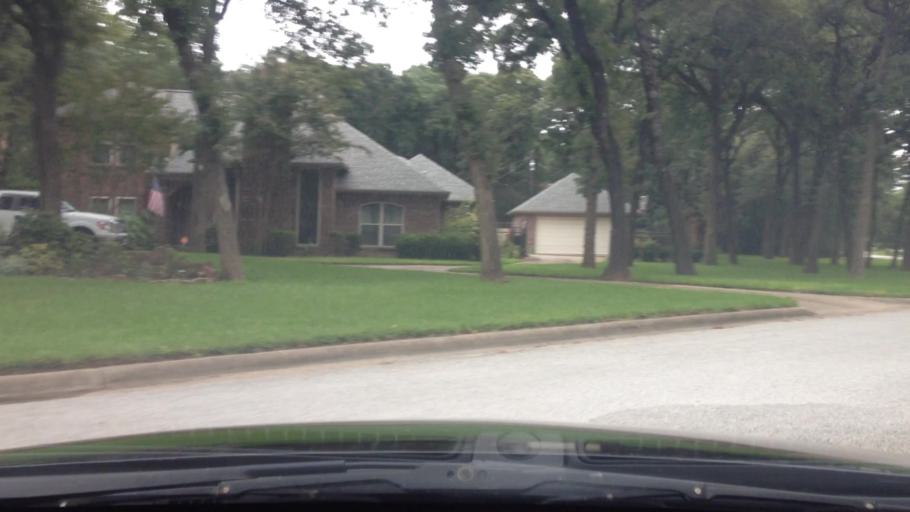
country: US
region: Texas
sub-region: Denton County
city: Trophy Club
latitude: 32.9545
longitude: -97.1969
